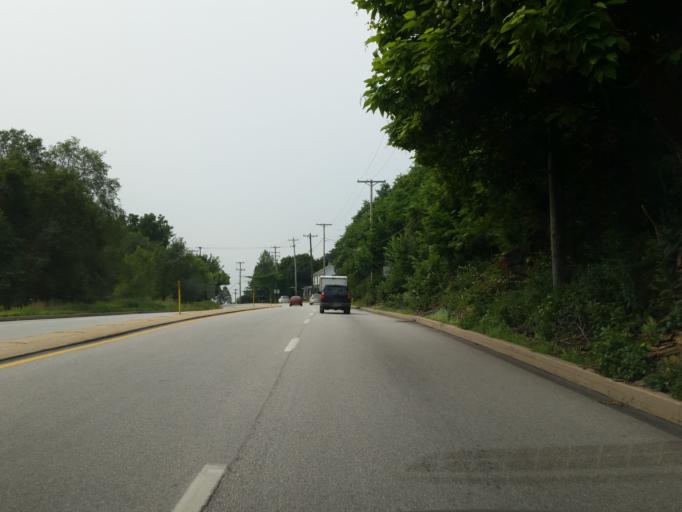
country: US
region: Pennsylvania
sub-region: York County
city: North York
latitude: 39.9887
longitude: -76.7359
